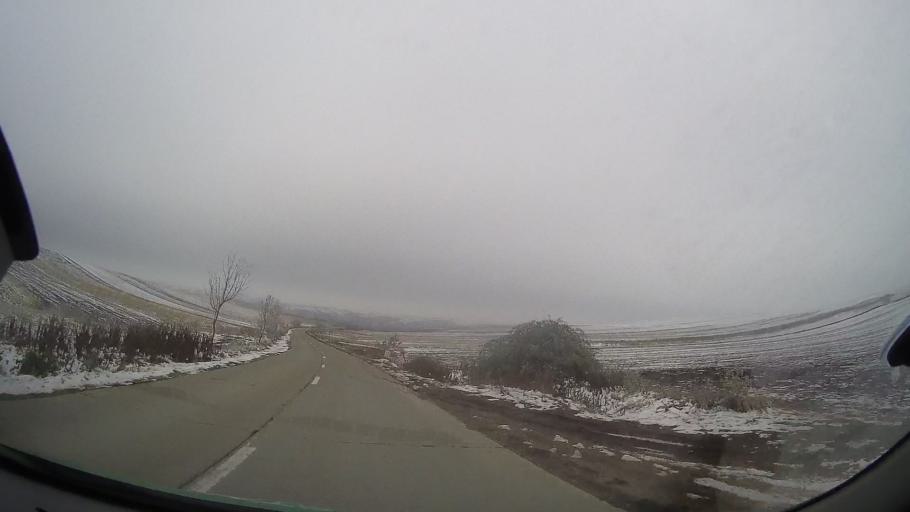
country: RO
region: Vaslui
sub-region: Comuna Ivesti
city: Ivesti
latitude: 46.2002
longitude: 27.5107
